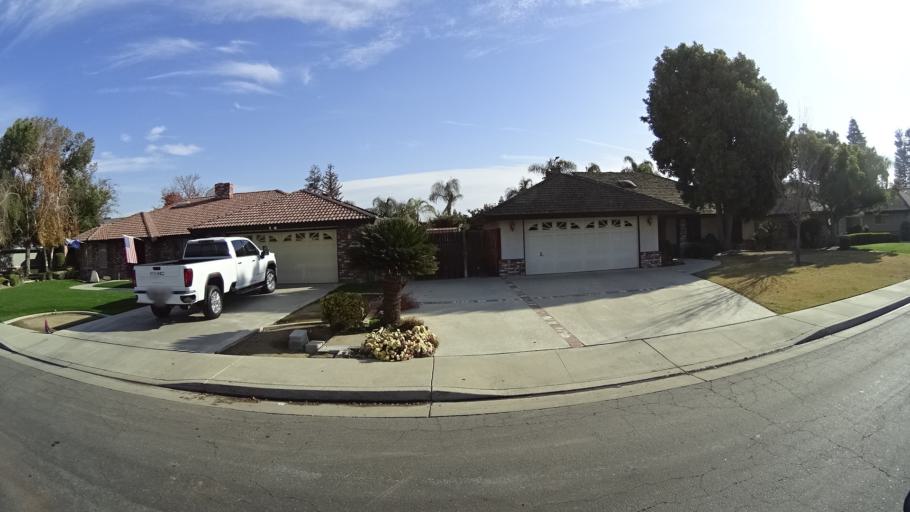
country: US
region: California
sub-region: Kern County
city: Greenacres
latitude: 35.4079
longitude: -119.0720
